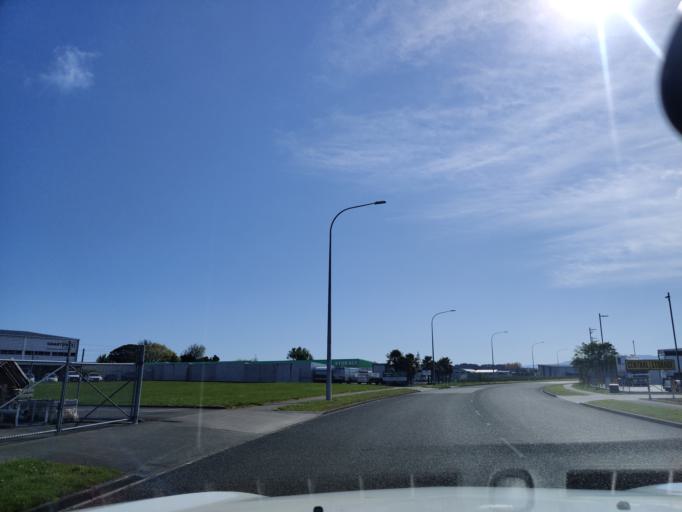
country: NZ
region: Manawatu-Wanganui
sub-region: Palmerston North City
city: Palmerston North
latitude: -40.3341
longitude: 175.6452
